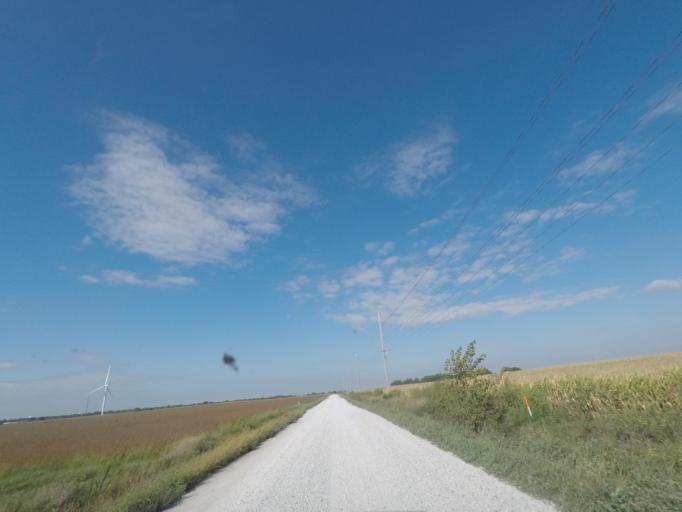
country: US
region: Iowa
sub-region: Story County
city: Nevada
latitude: 42.0345
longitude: -93.4166
